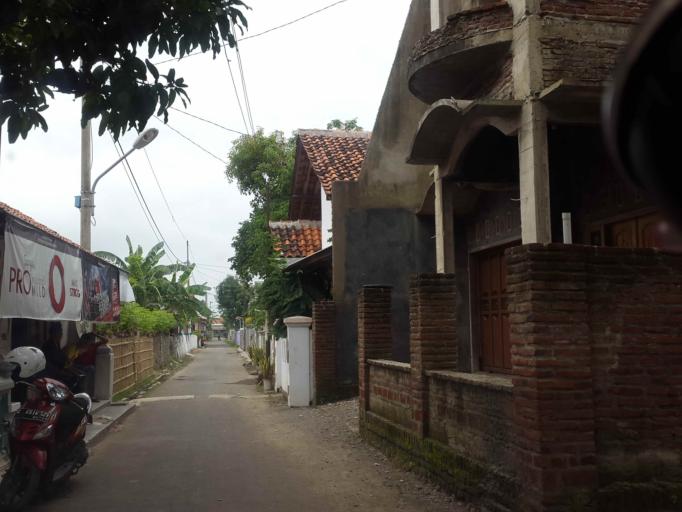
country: ID
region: Central Java
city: Dukuhturi
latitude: -6.8769
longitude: 109.0874
